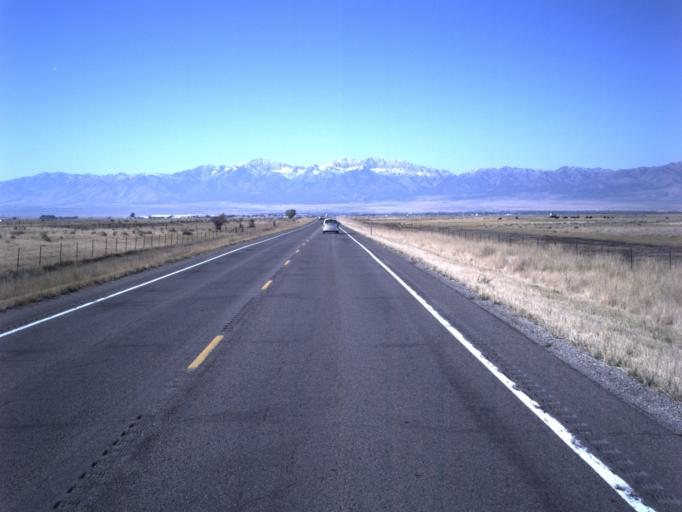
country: US
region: Utah
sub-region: Tooele County
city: Erda
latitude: 40.6300
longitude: -112.3406
